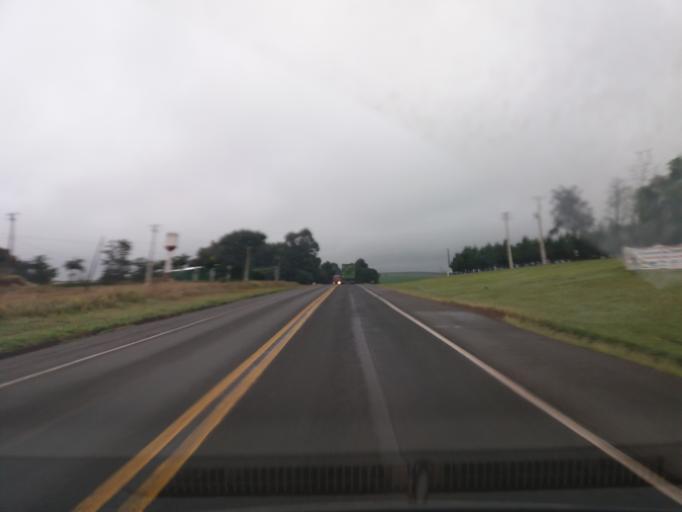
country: BR
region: Parana
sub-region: Ampere
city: Ampere
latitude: -25.9073
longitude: -53.4391
